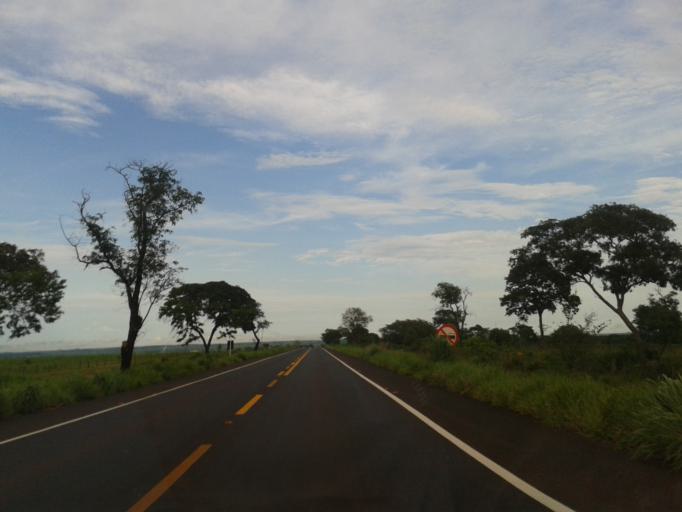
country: BR
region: Minas Gerais
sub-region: Santa Vitoria
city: Santa Vitoria
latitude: -19.0443
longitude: -50.4499
